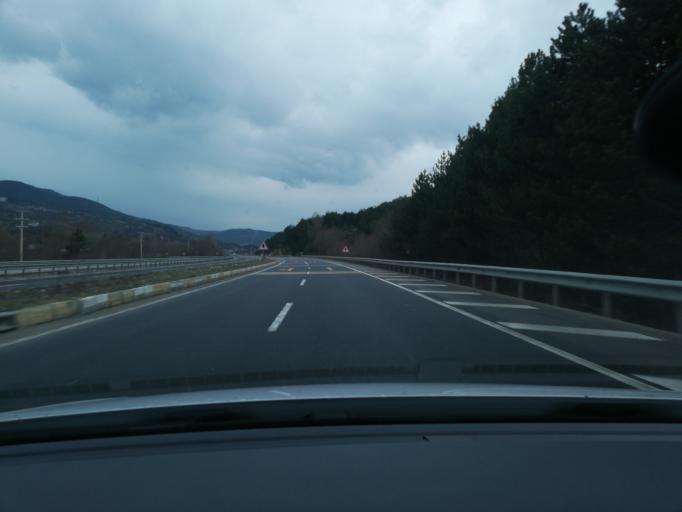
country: TR
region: Bolu
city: Yenicaga
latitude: 40.7446
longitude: 31.8549
